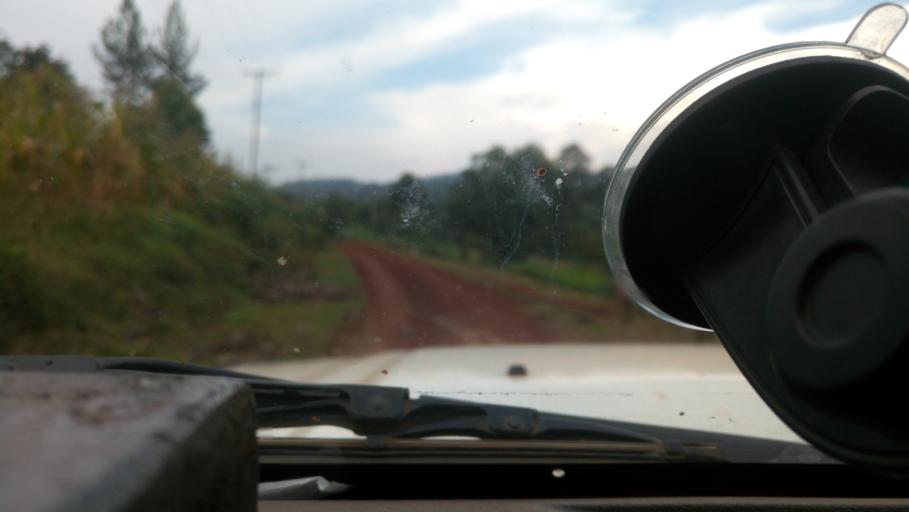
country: KE
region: Kisii
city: Ogembo
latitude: -0.8946
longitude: 34.7899
